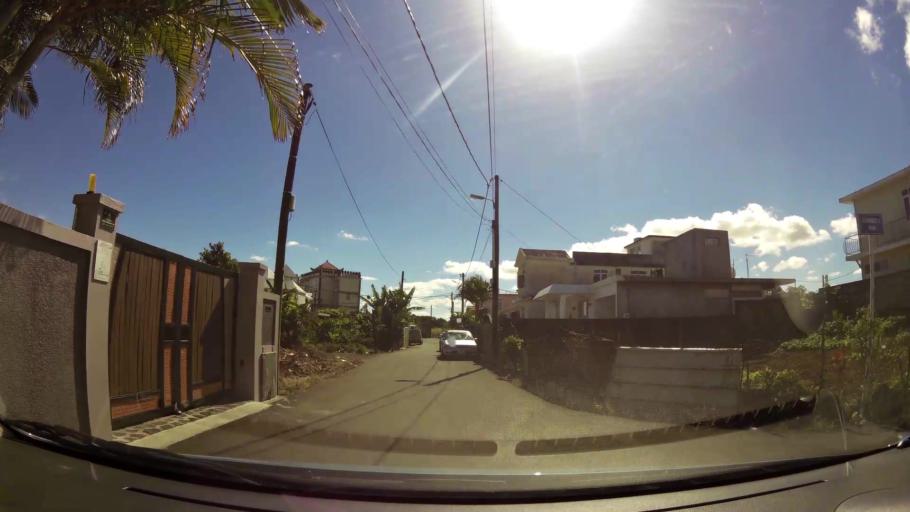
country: MU
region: Plaines Wilhems
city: Vacoas
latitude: -20.3338
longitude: 57.4781
